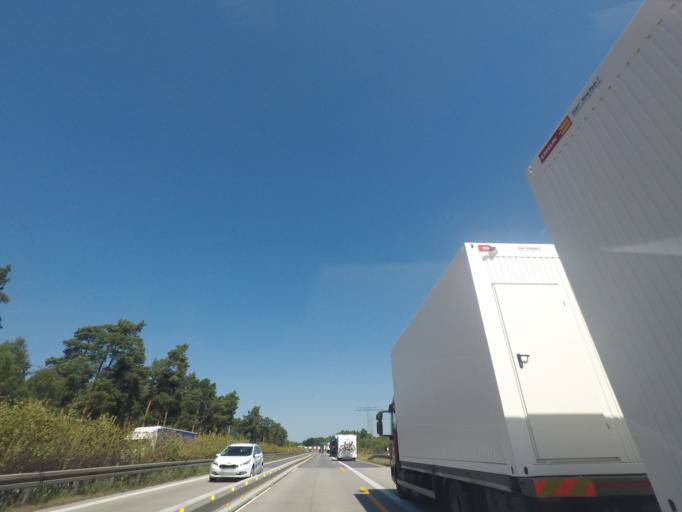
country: DE
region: Brandenburg
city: Schwerin
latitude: 52.1496
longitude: 13.6492
